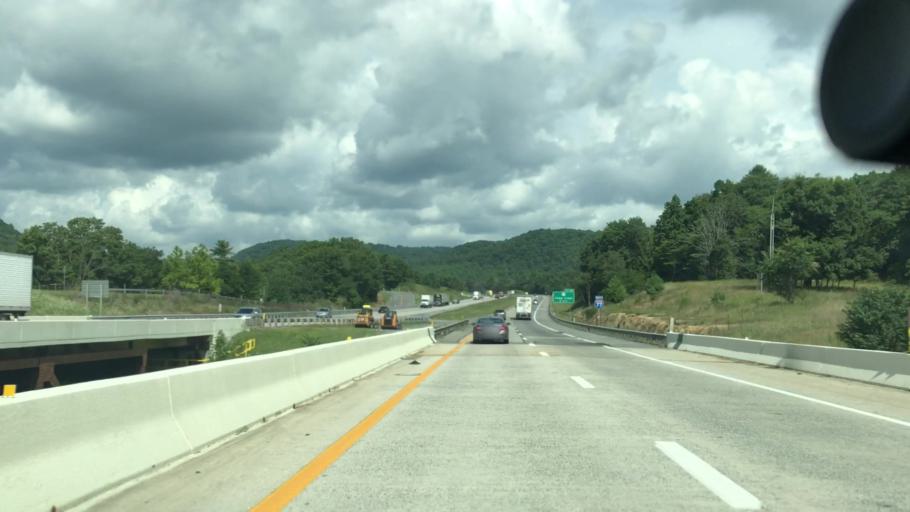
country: US
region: West Virginia
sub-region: Mercer County
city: Athens
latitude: 37.4806
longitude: -81.0742
